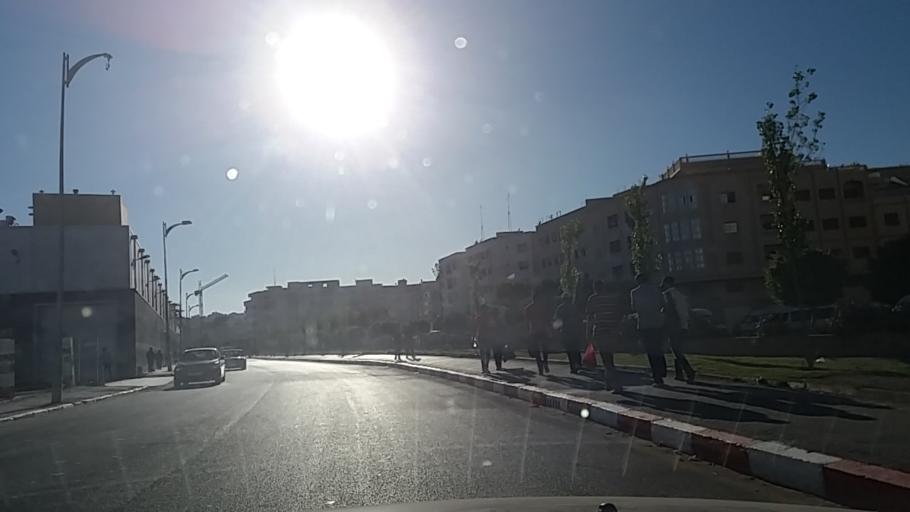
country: MA
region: Tanger-Tetouan
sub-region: Tanger-Assilah
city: Tangier
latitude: 35.7365
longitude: -5.7978
